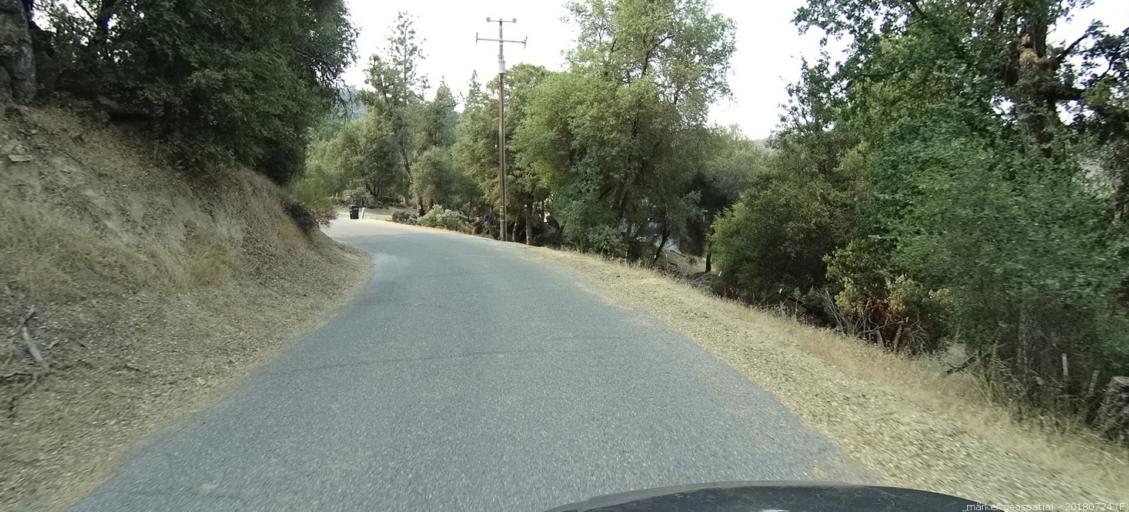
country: US
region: California
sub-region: Madera County
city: Oakhurst
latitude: 37.3186
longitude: -119.6235
